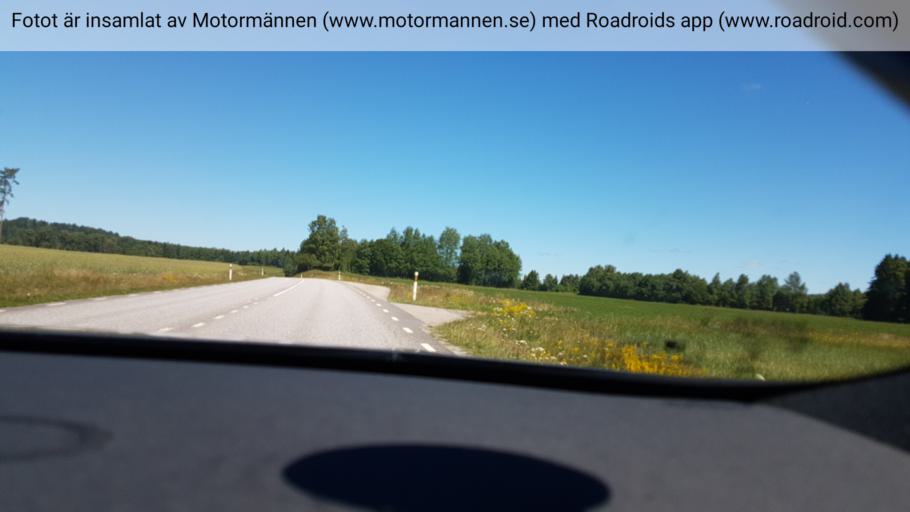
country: SE
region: Vaestra Goetaland
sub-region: Ulricehamns Kommun
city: Ulricehamn
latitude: 57.8737
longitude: 13.4334
